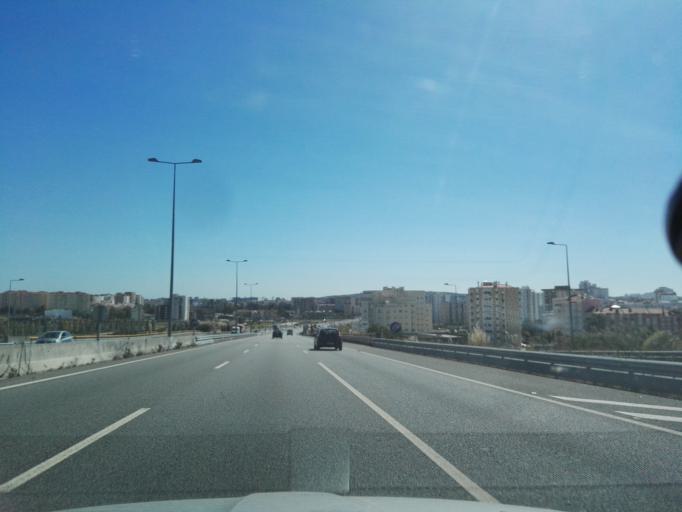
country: PT
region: Lisbon
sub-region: Odivelas
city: Olival do Basto
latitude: 38.7848
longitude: -9.1544
